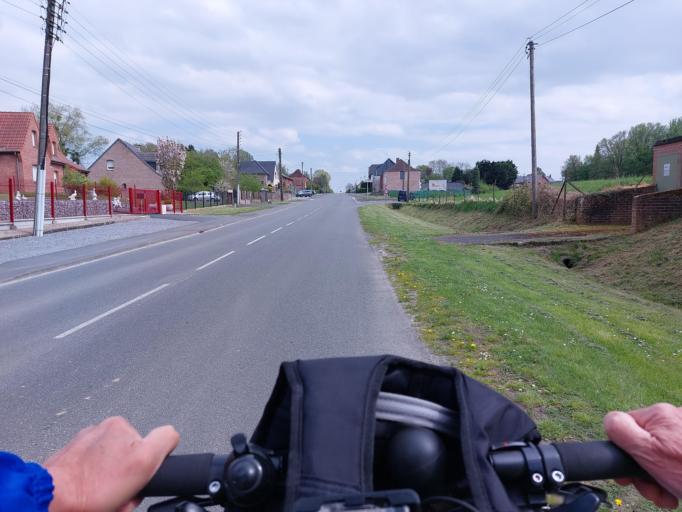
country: FR
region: Nord-Pas-de-Calais
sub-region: Departement du Nord
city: La Longueville
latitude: 50.2860
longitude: 3.8624
